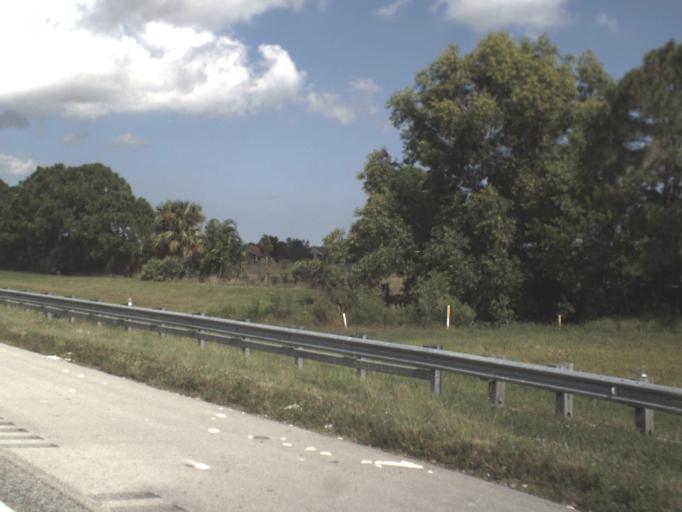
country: US
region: Florida
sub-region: Saint Lucie County
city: White City
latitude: 27.3521
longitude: -80.3742
